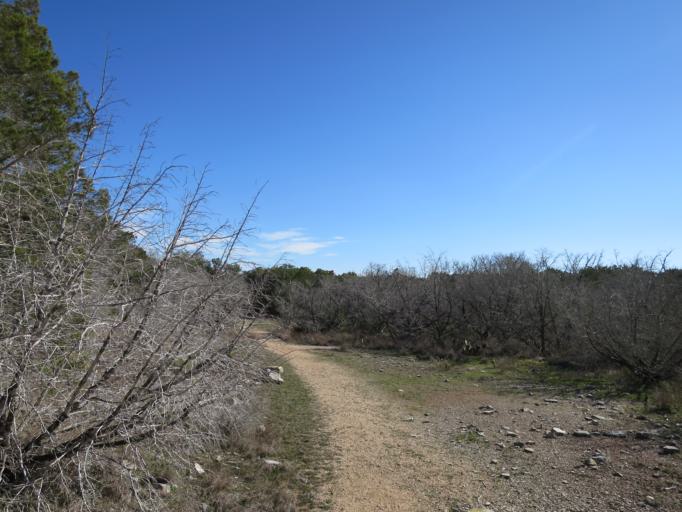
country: US
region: Texas
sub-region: Llano County
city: Kingsland
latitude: 30.6828
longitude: -98.3552
